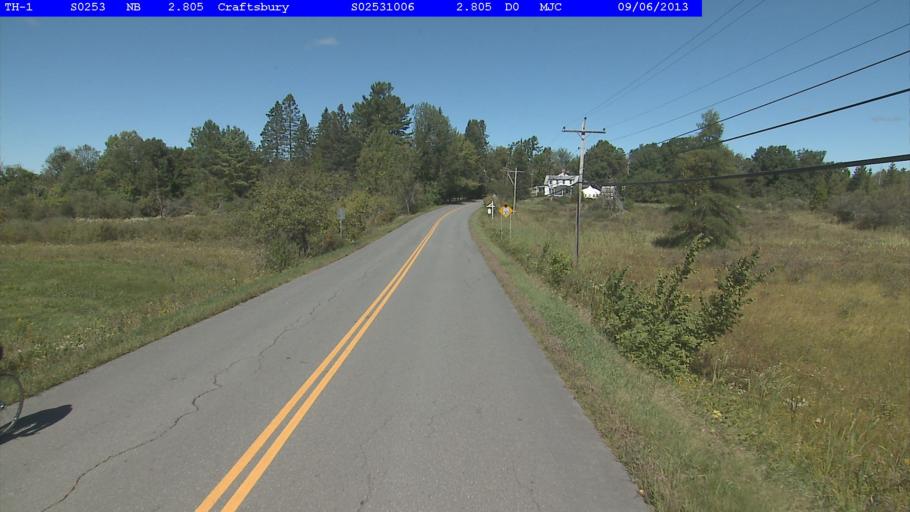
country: US
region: Vermont
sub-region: Caledonia County
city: Hardwick
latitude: 44.6487
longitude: -72.3807
